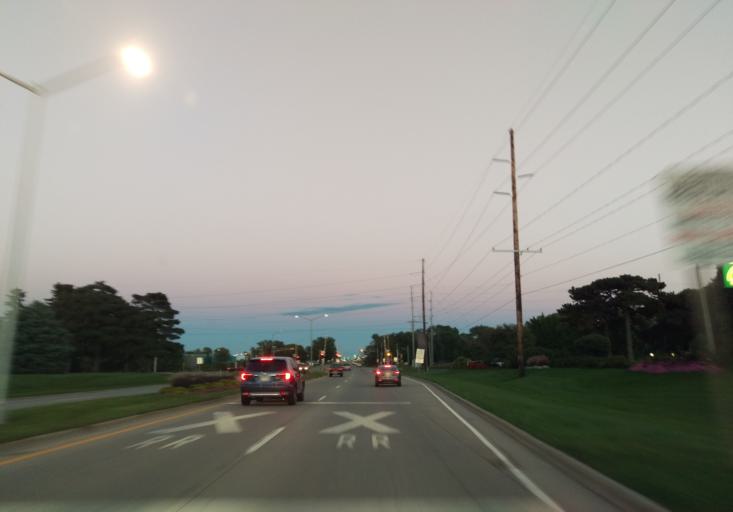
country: US
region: Wisconsin
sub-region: Rock County
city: Janesville
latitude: 42.7233
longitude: -89.0083
